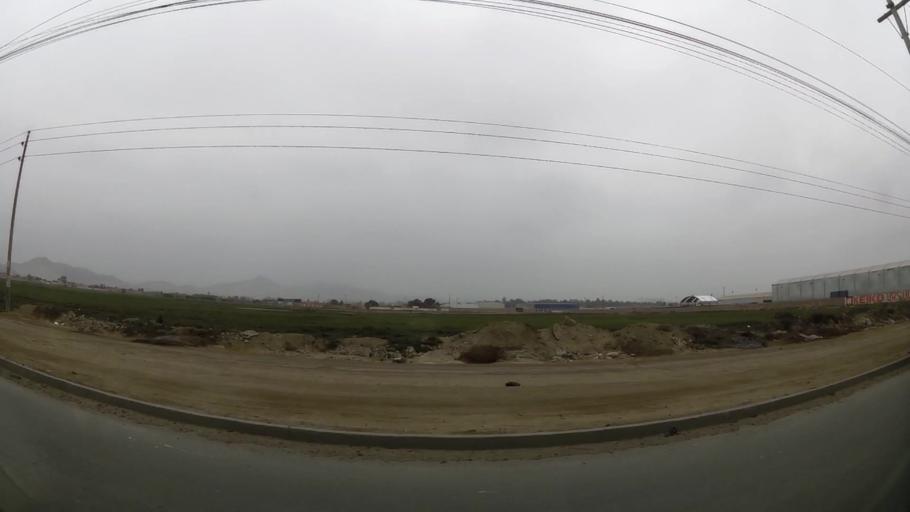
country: PE
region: Lima
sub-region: Lima
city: Punta Hermosa
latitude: -12.2877
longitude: -76.8597
